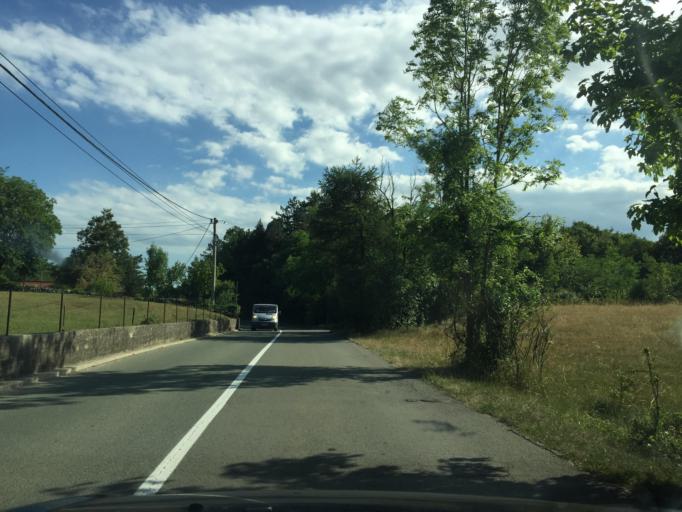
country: HR
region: Primorsko-Goranska
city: Klana
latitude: 45.4392
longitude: 14.3664
